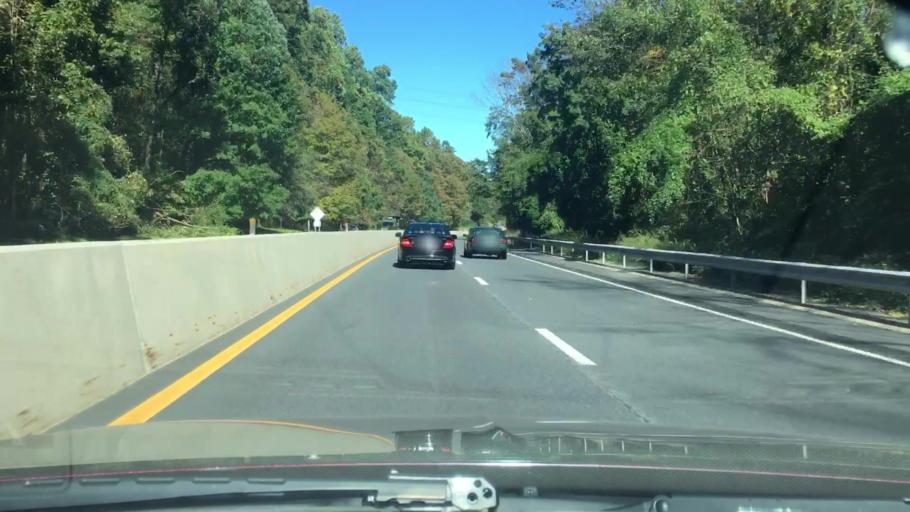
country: US
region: New York
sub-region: Westchester County
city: Pleasantville
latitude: 41.1437
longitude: -73.7897
